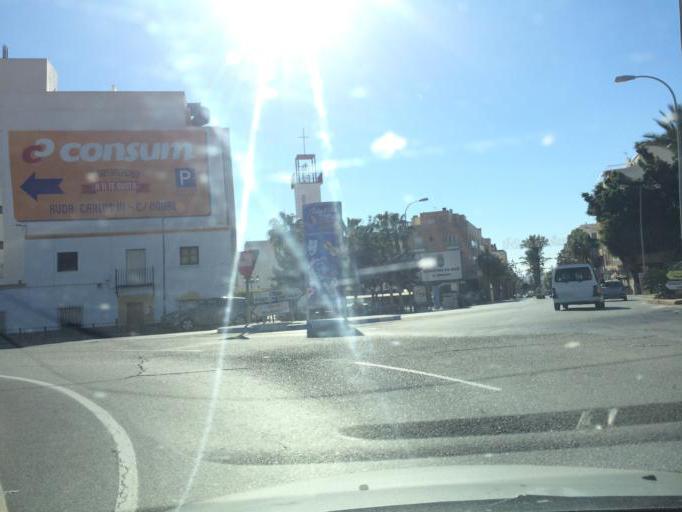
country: ES
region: Andalusia
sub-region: Provincia de Almeria
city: Aguadulce
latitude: 36.8090
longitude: -2.5976
